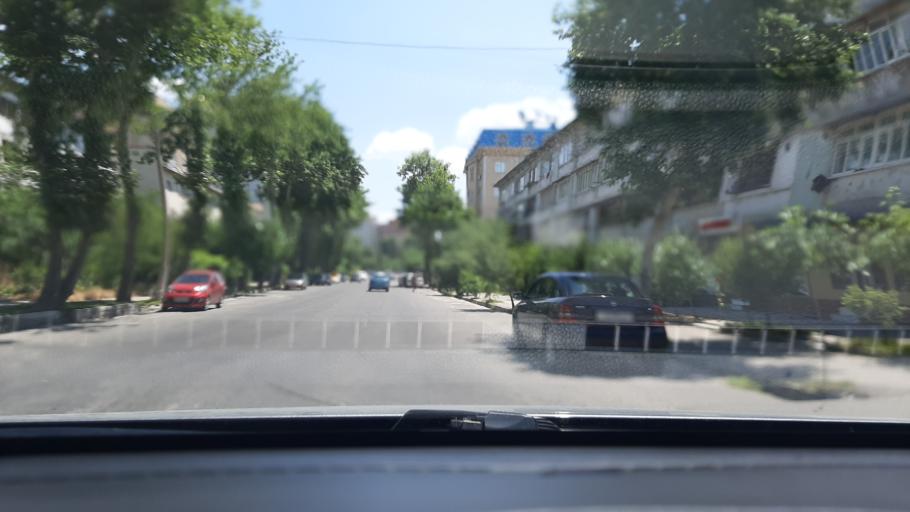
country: TJ
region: Dushanbe
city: Dushanbe
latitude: 38.5330
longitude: 68.7665
